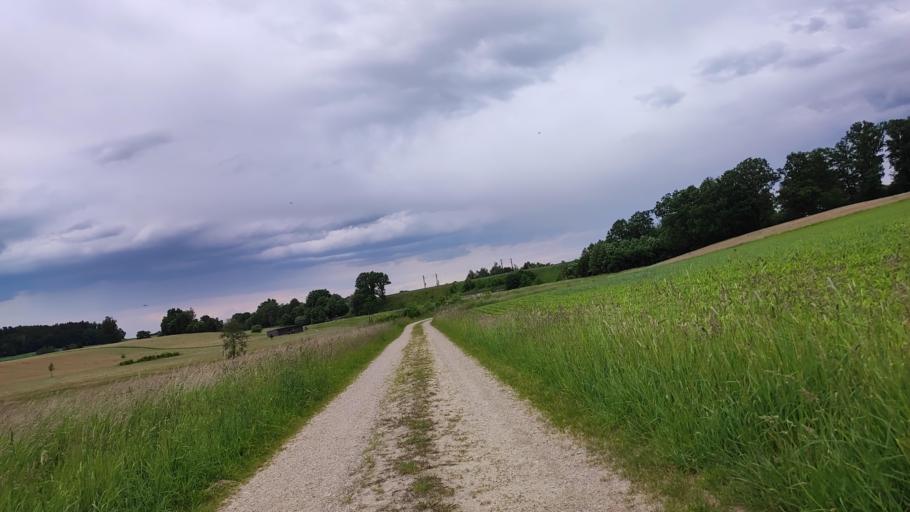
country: DE
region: Bavaria
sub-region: Swabia
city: Dinkelscherben
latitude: 48.3576
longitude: 10.5565
